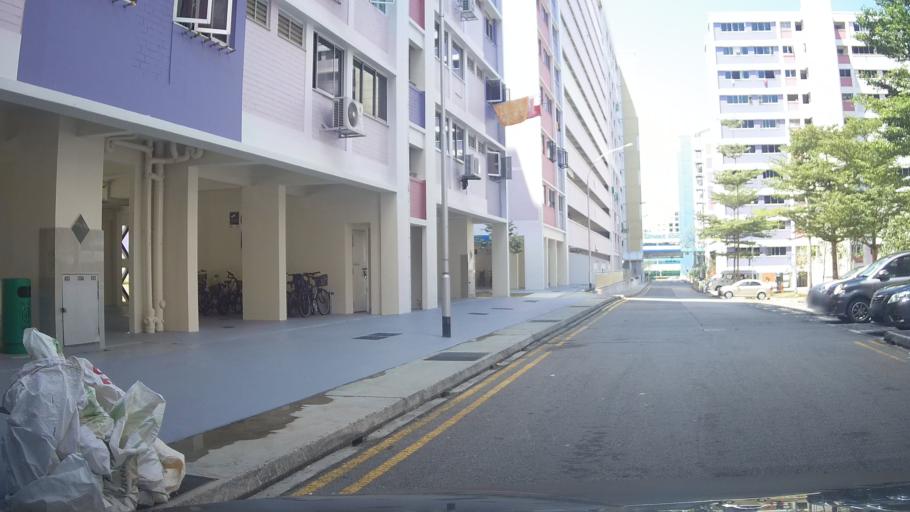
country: MY
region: Johor
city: Kampung Pasir Gudang Baru
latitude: 1.3746
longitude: 103.9581
